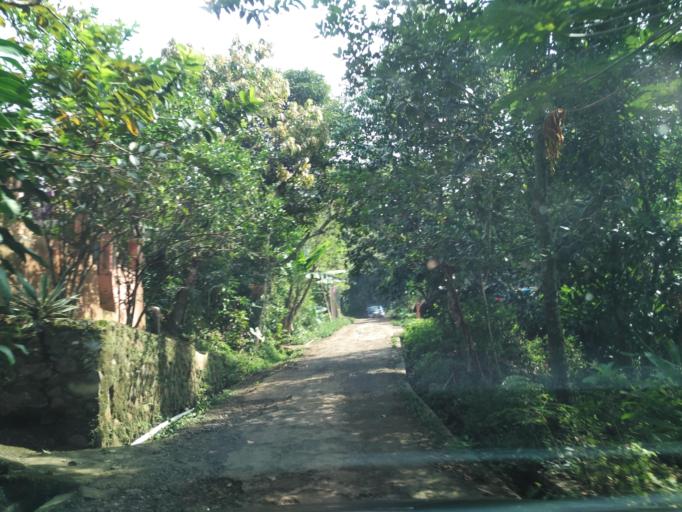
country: ID
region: West Java
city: Ciranjang-hilir
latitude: -6.7867
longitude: 107.1245
